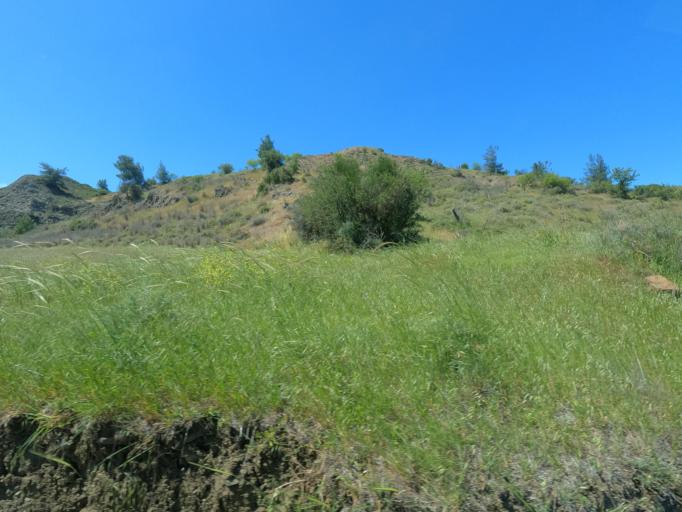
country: CY
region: Lefkosia
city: Peristerona
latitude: 35.0506
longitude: 33.0762
